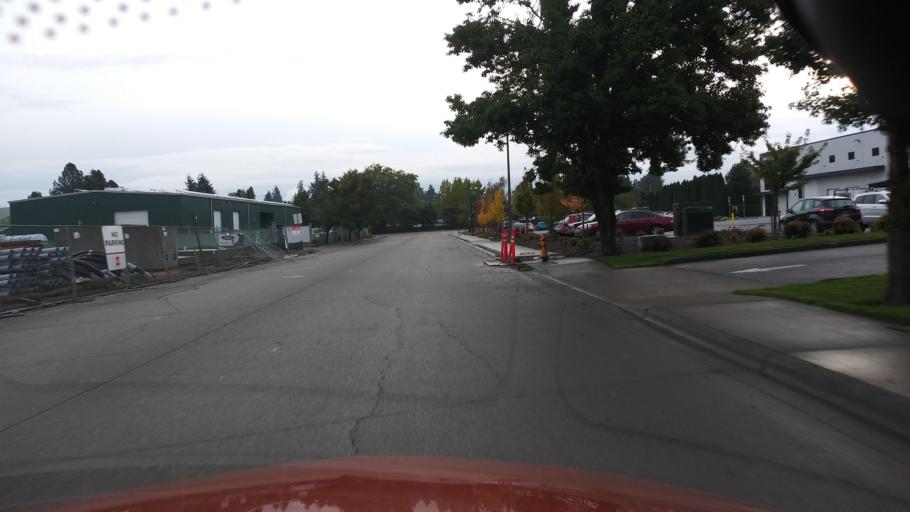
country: US
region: Oregon
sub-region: Washington County
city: Cornelius
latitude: 45.5265
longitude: -123.0616
